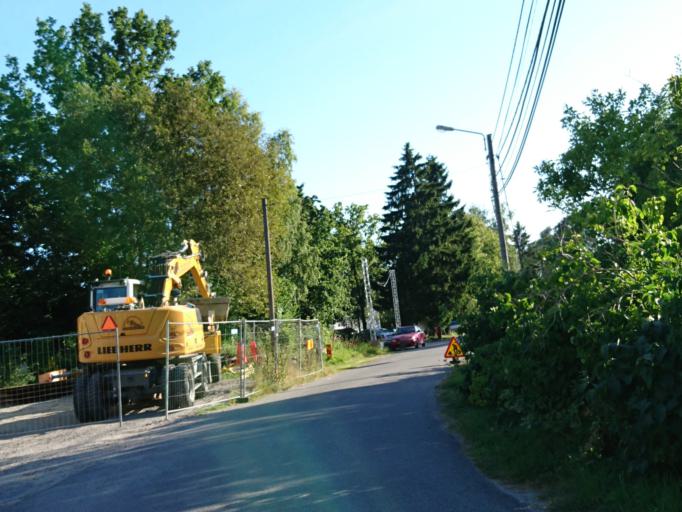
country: SE
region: Stockholm
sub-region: Huddinge Kommun
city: Segeltorp
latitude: 59.2785
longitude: 17.9331
